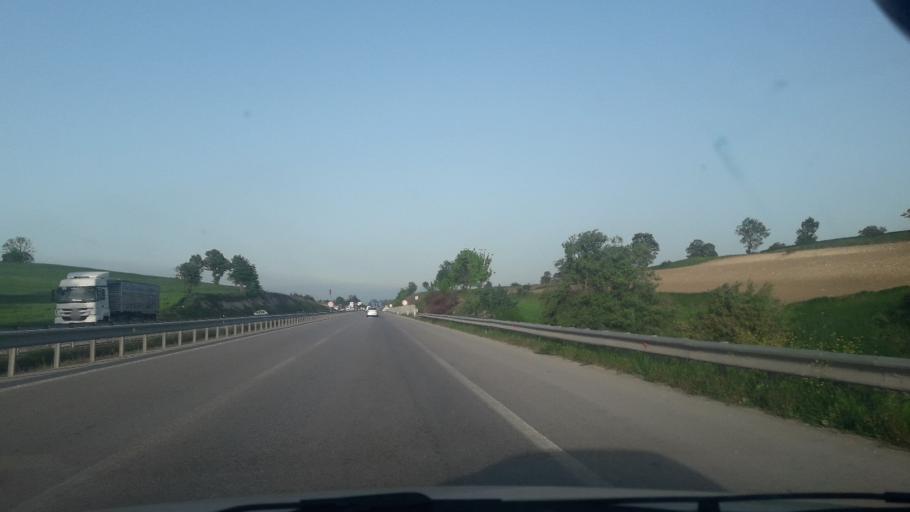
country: TR
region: Samsun
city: Havza
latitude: 40.9976
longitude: 35.7699
